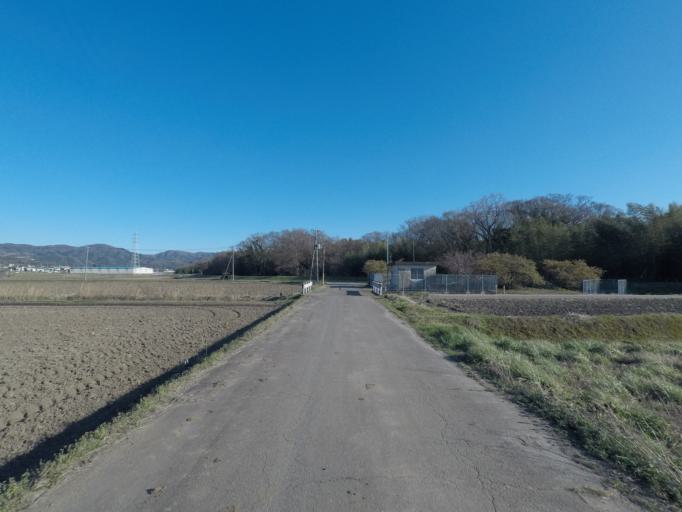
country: JP
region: Ibaraki
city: Tsukuba
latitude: 36.2104
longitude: 140.0665
